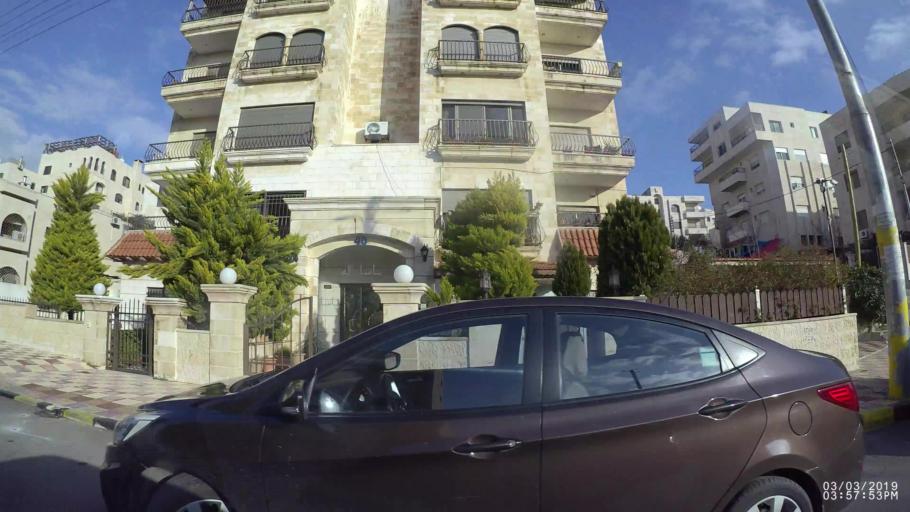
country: JO
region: Amman
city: Al Jubayhah
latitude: 31.9851
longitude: 35.8700
